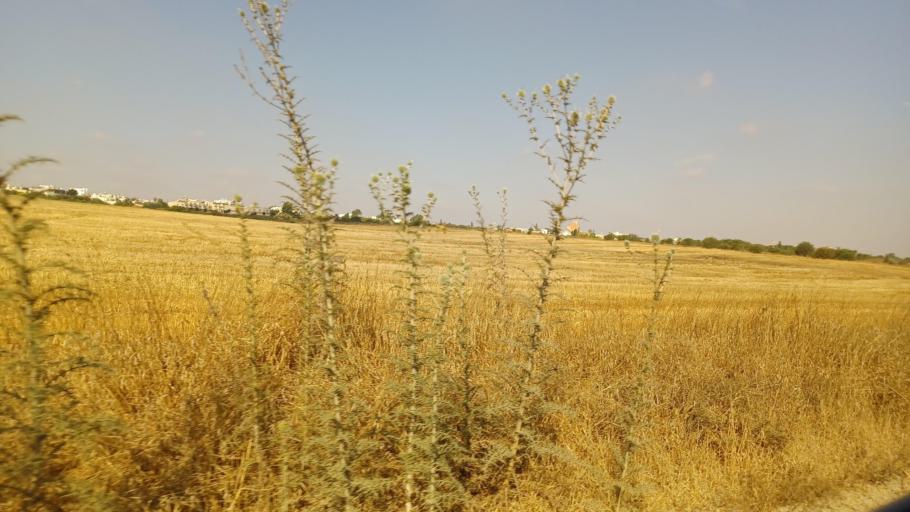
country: CY
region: Ammochostos
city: Deryneia
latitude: 35.0674
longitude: 33.9743
